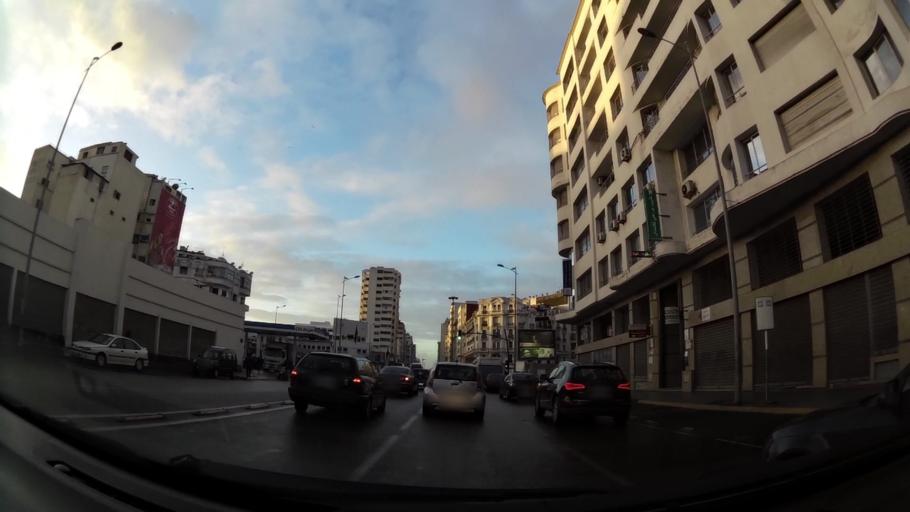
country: MA
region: Grand Casablanca
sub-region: Casablanca
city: Casablanca
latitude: 33.5894
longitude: -7.6038
